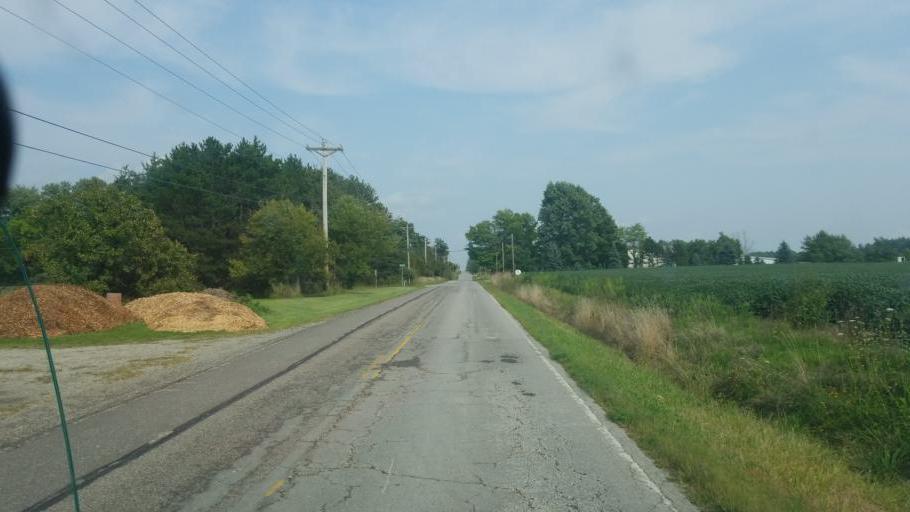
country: US
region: Ohio
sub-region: Medina County
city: Lodi
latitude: 41.1362
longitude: -82.0455
